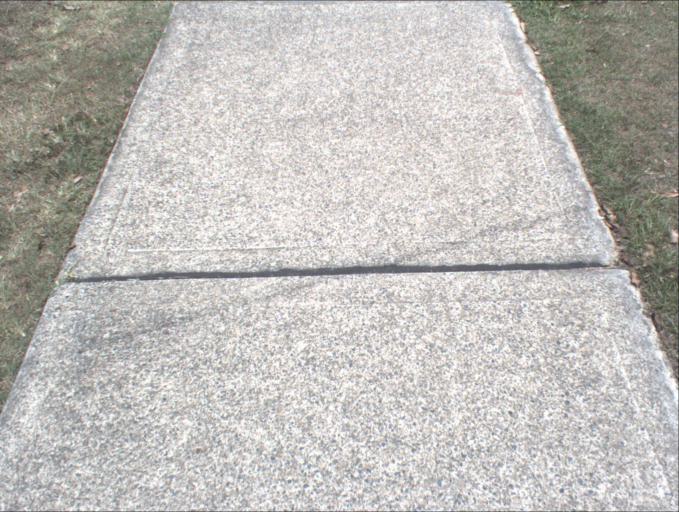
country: AU
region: Queensland
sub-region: Logan
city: Windaroo
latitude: -27.7334
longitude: 153.2081
